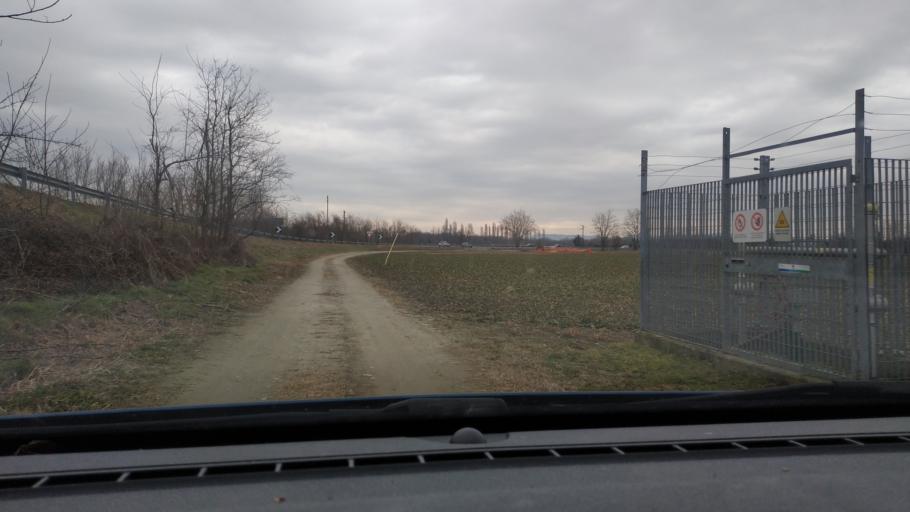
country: IT
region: Piedmont
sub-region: Provincia di Torino
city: Ivrea
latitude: 45.4563
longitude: 7.8841
